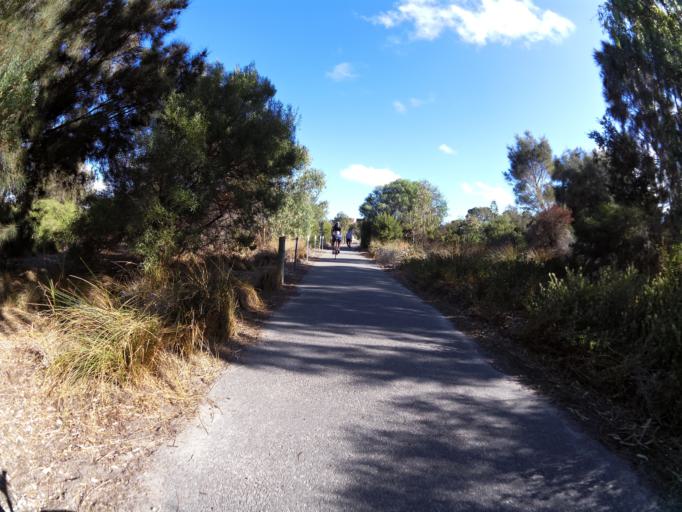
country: AU
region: Western Australia
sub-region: East Fremantle
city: East Fremantle
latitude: -32.0367
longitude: 115.7586
